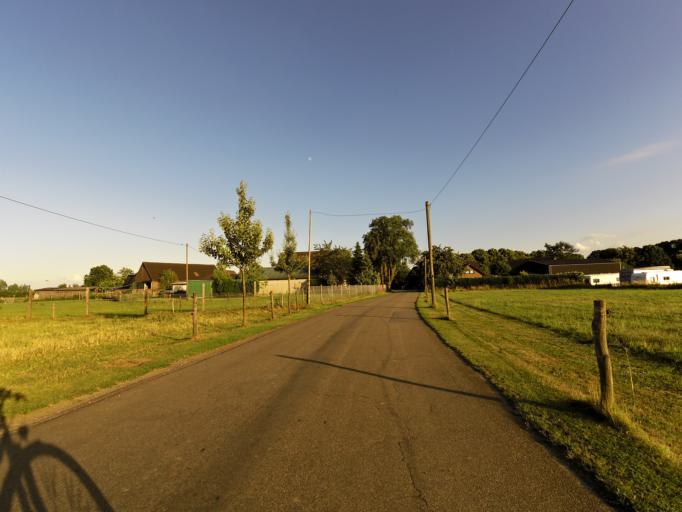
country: DE
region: North Rhine-Westphalia
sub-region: Regierungsbezirk Munster
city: Isselburg
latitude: 51.8595
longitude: 6.4346
